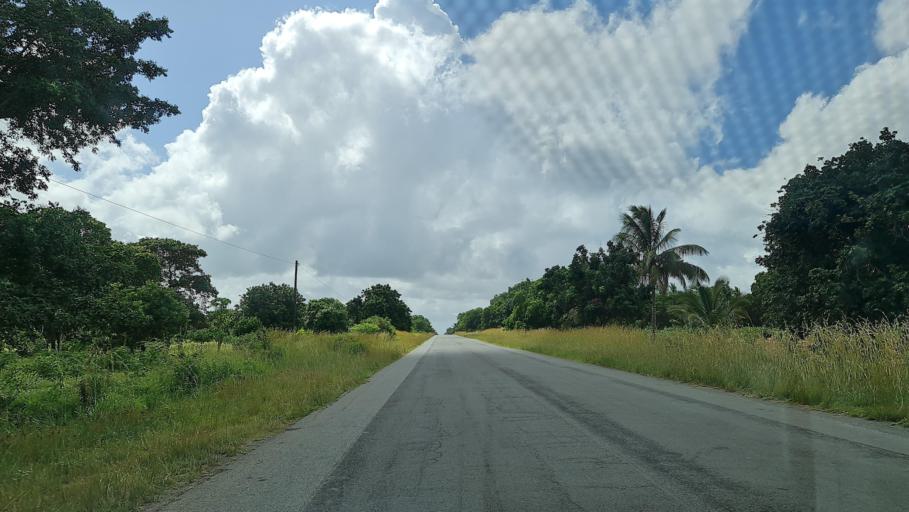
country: MZ
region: Gaza
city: Manjacaze
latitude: -24.6787
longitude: 34.5974
